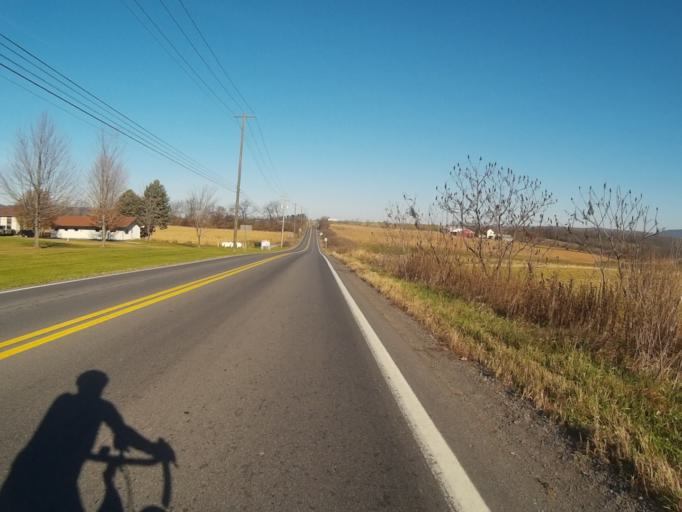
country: US
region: Pennsylvania
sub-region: Centre County
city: Houserville
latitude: 40.8394
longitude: -77.8724
